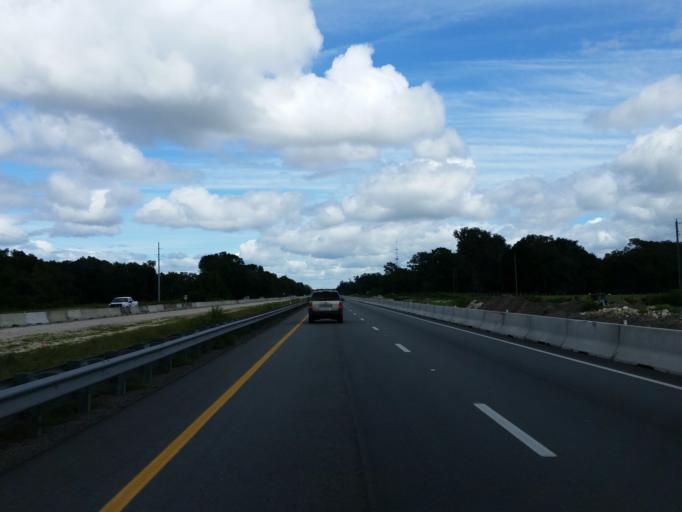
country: US
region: Florida
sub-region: Sumter County
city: Bushnell
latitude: 28.6961
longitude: -82.1277
